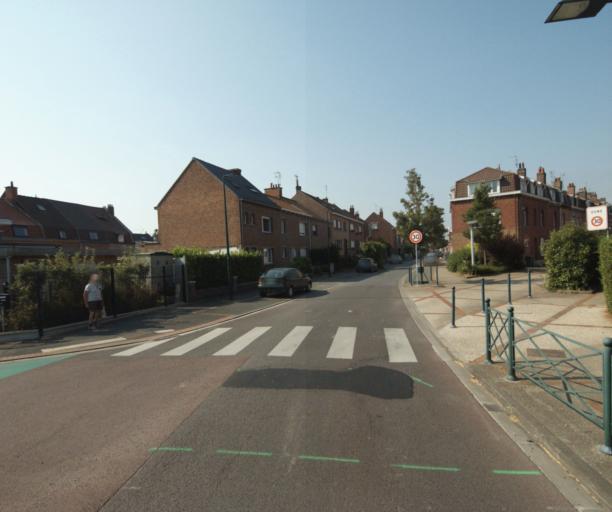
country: FR
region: Nord-Pas-de-Calais
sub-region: Departement du Nord
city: Quesnoy-sur-Deule
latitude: 50.7142
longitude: 3.0008
